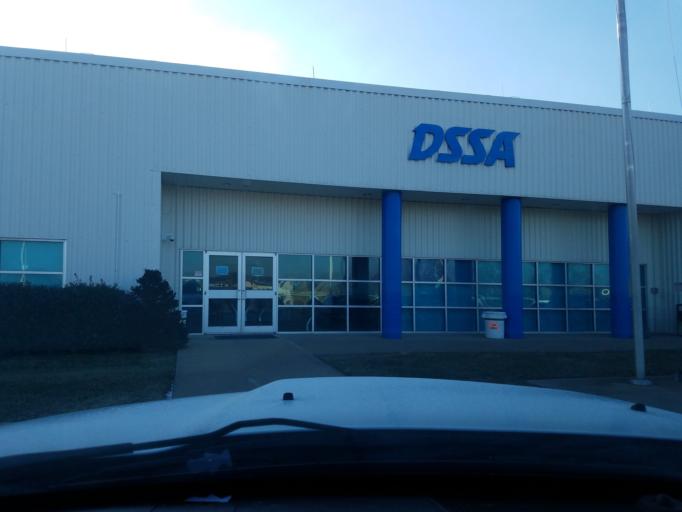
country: US
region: Kentucky
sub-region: Ohio County
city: Beaver Dam
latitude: 37.3736
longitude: -86.8272
